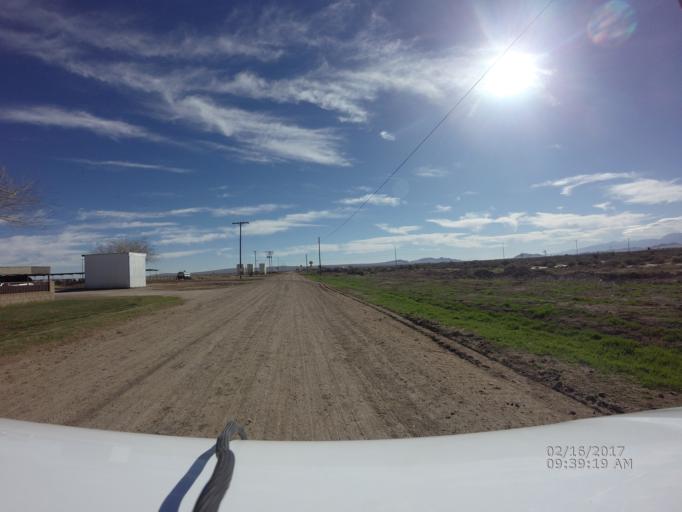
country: US
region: California
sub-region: Kern County
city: Edwards Air Force Base
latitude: 34.7415
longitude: -117.9537
